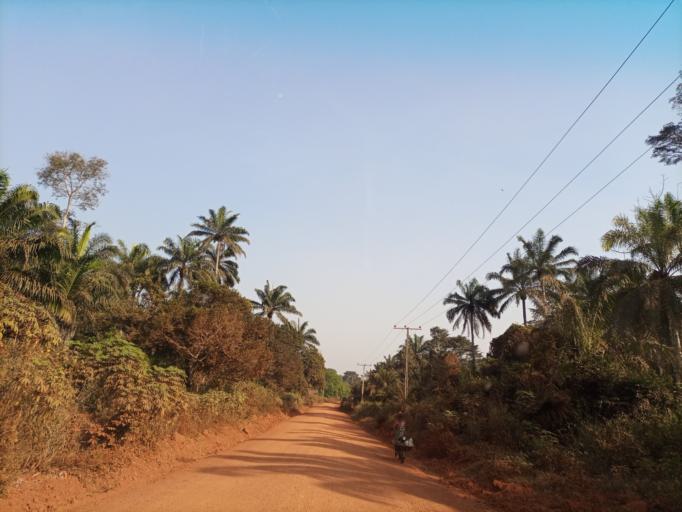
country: NG
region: Enugu
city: Opi
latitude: 6.7600
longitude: 7.3998
